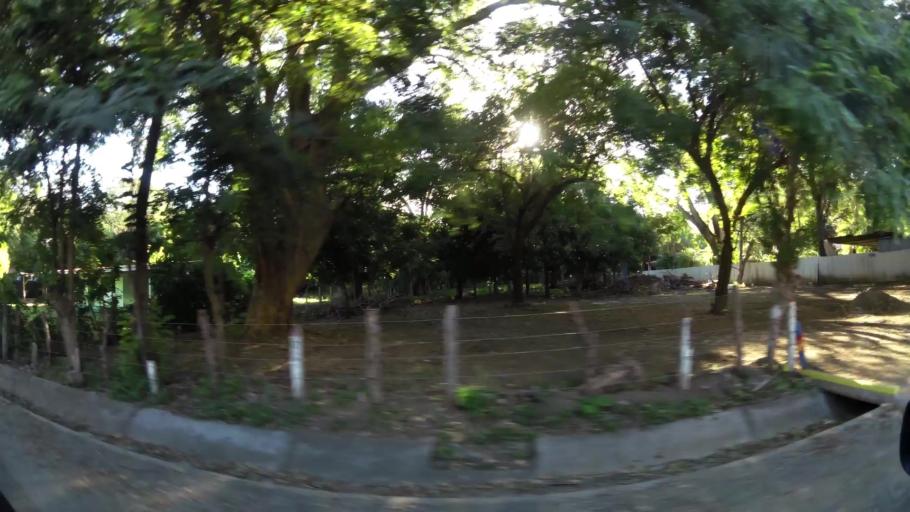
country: CR
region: Guanacaste
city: Sardinal
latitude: 10.5778
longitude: -85.6762
